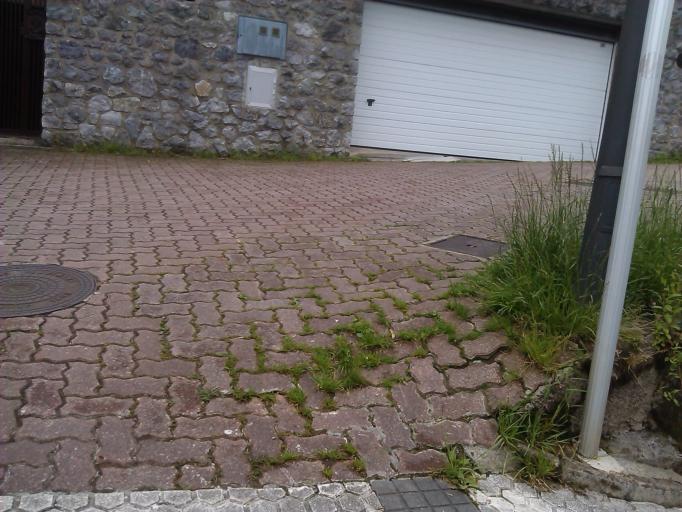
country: ES
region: Basque Country
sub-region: Provincia de Guipuzcoa
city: Andoain
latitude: 43.2137
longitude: -2.0192
